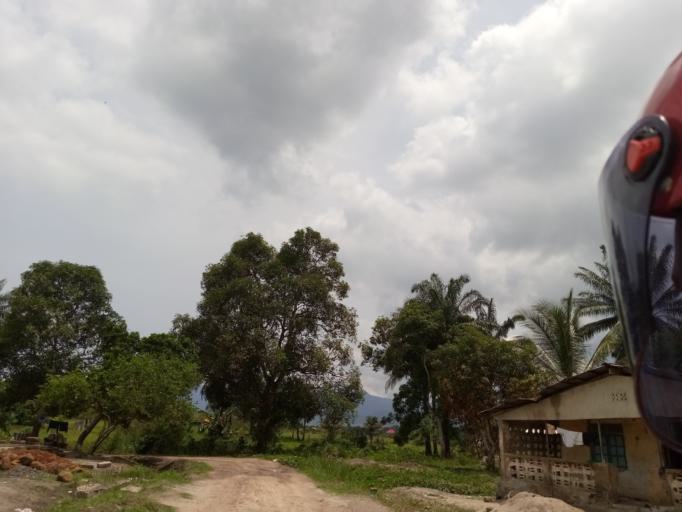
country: SL
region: Western Area
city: Waterloo
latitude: 8.3200
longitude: -13.0343
